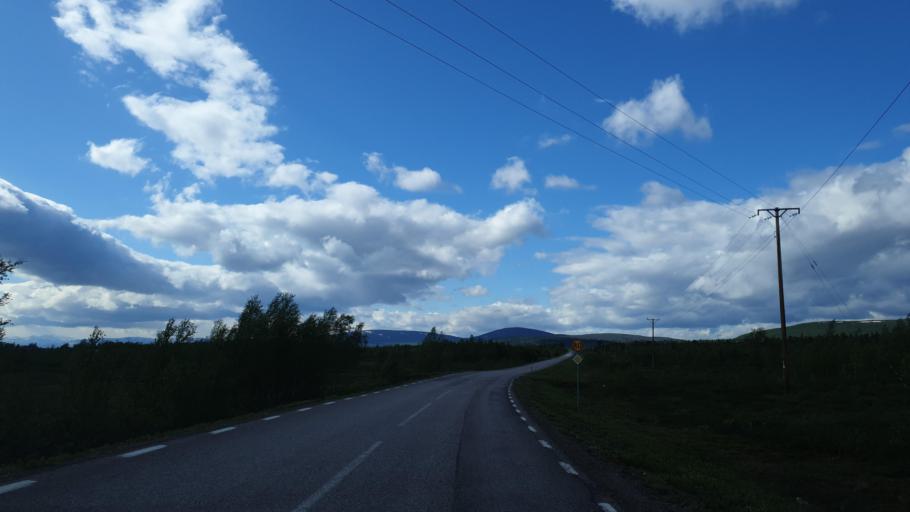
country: SE
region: Norrbotten
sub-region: Kiruna Kommun
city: Kiruna
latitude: 67.7680
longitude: 19.9810
